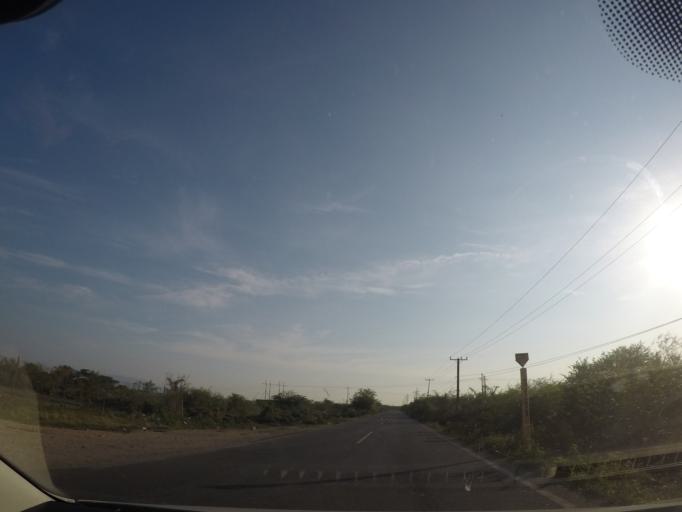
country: MX
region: Oaxaca
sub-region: Santo Domingo Tehuantepec
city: La Noria
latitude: 16.2265
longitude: -95.1866
